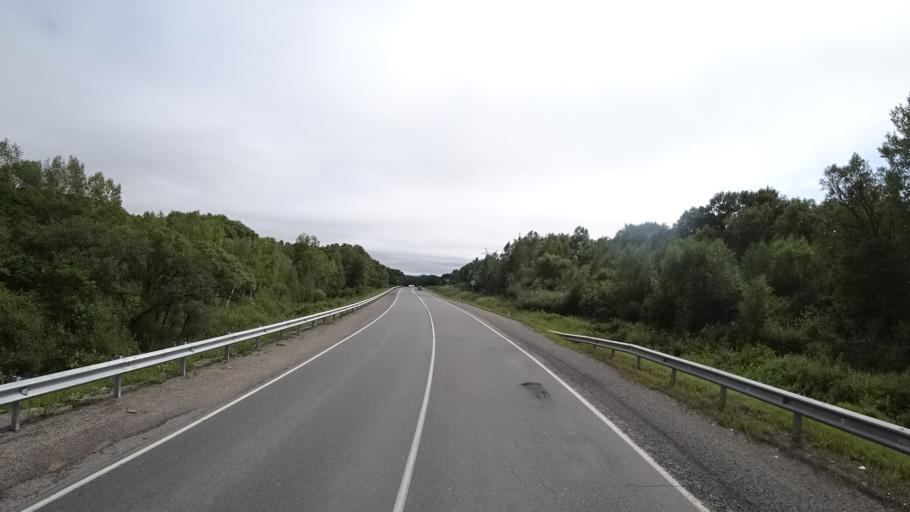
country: RU
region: Primorskiy
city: Lyalichi
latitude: 44.1101
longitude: 132.4199
